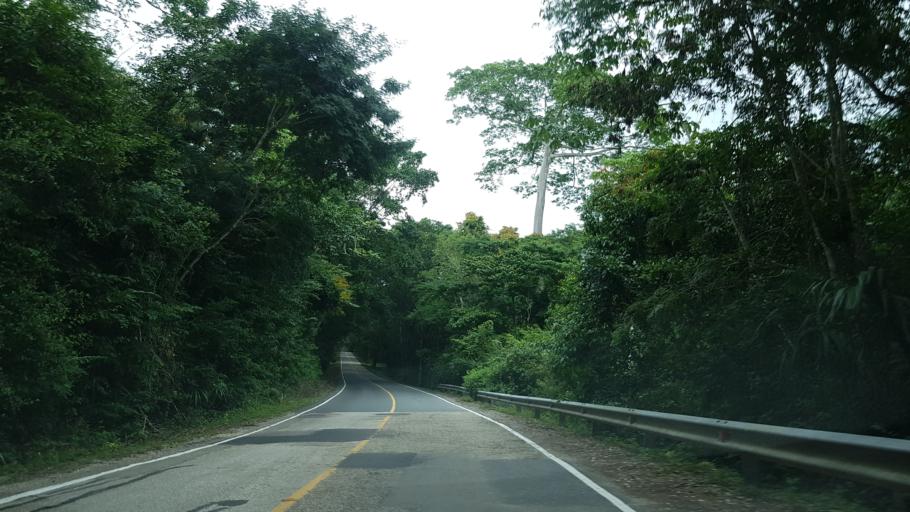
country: GT
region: Peten
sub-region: Municipio de San Jose
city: San Jose
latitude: 17.1815
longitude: -89.6341
